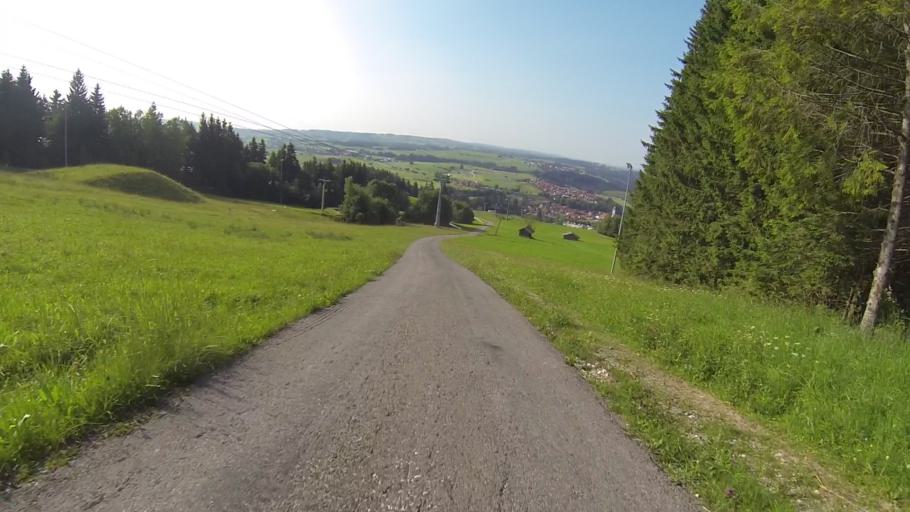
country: DE
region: Bavaria
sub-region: Swabia
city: Nesselwang
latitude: 47.6122
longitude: 10.4978
